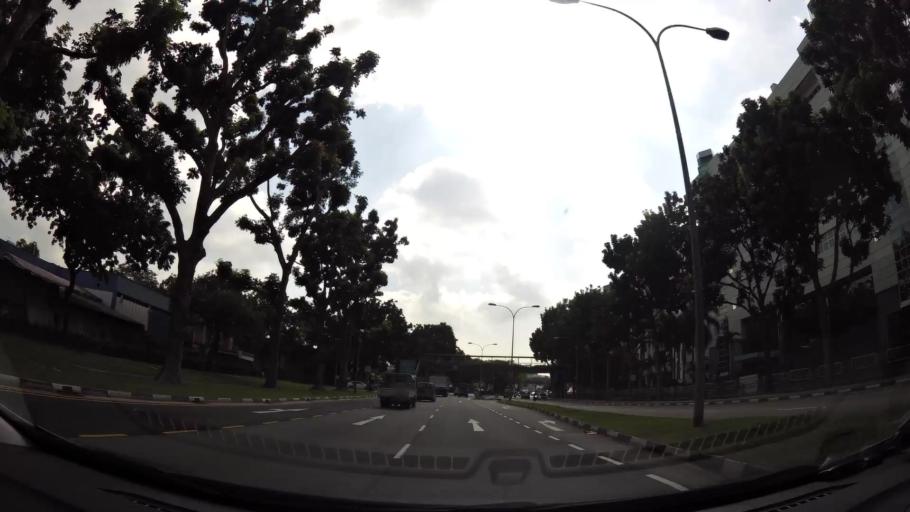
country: SG
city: Singapore
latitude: 1.3395
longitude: 103.8938
